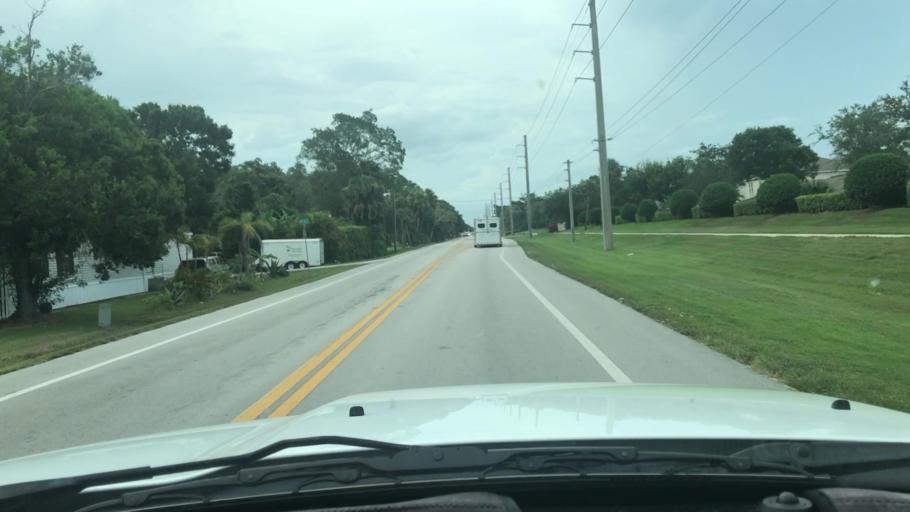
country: US
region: Florida
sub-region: Indian River County
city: Florida Ridge
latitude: 27.5804
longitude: -80.4143
